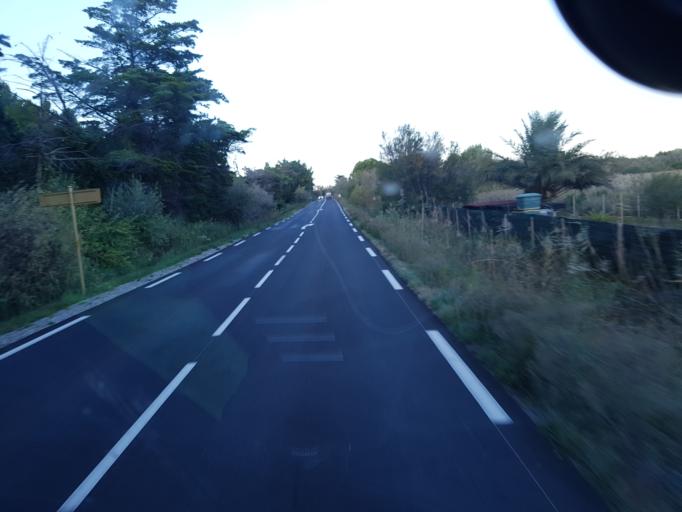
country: FR
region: Languedoc-Roussillon
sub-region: Departement de l'Aude
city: Port-la-Nouvelle
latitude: 42.9940
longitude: 3.0395
